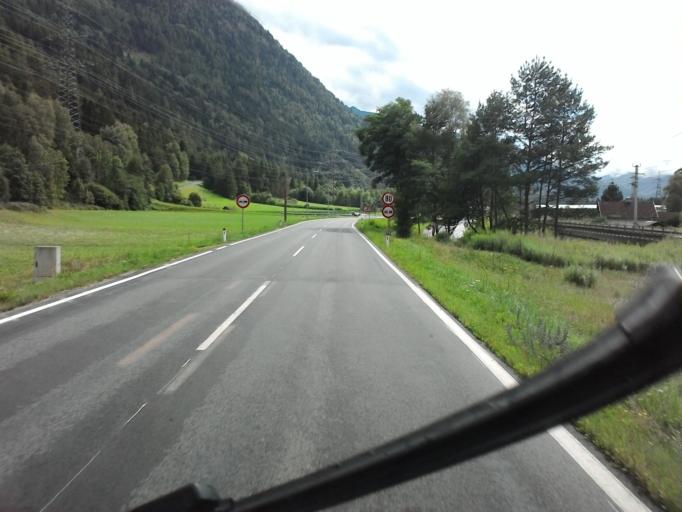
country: AT
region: Tyrol
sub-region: Politischer Bezirk Imst
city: Haiming
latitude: 47.2455
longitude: 10.8831
